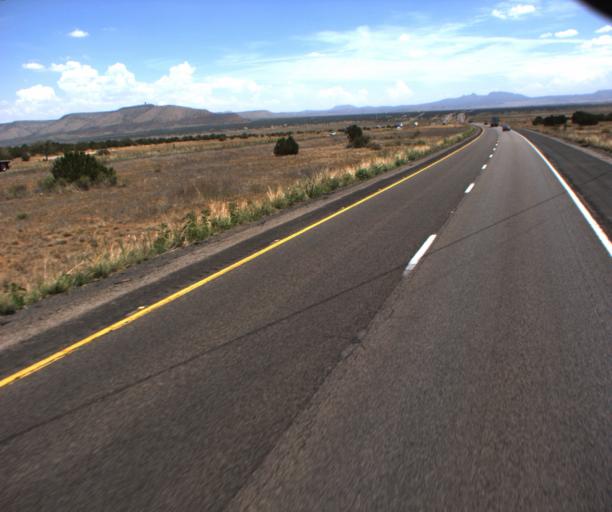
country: US
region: Arizona
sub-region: Mohave County
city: Peach Springs
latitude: 35.3037
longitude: -112.9977
